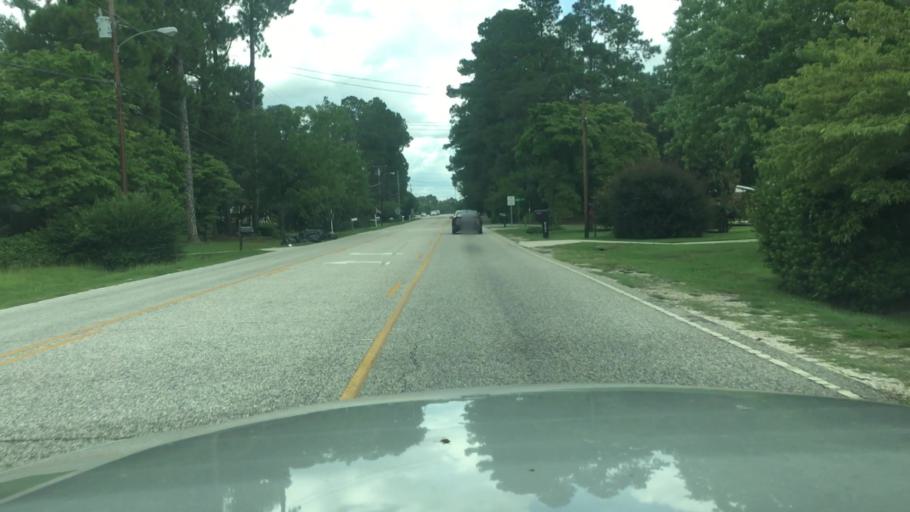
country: US
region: North Carolina
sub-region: Cumberland County
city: Hope Mills
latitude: 35.0398
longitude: -78.9849
